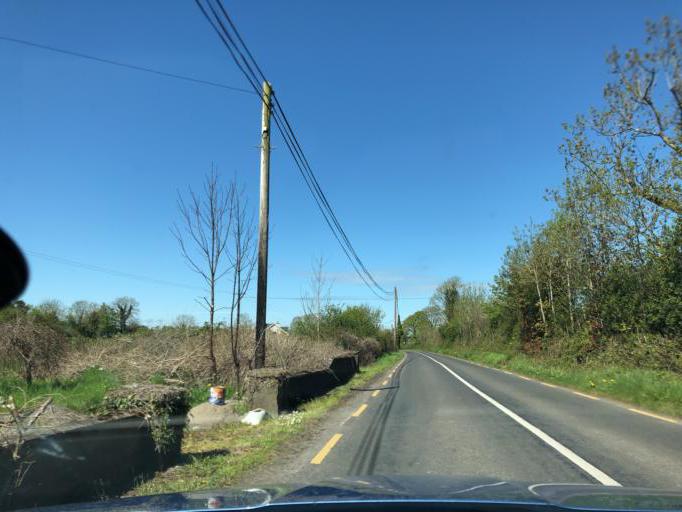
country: IE
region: Connaught
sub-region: County Galway
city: Portumna
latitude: 53.1259
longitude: -8.3372
